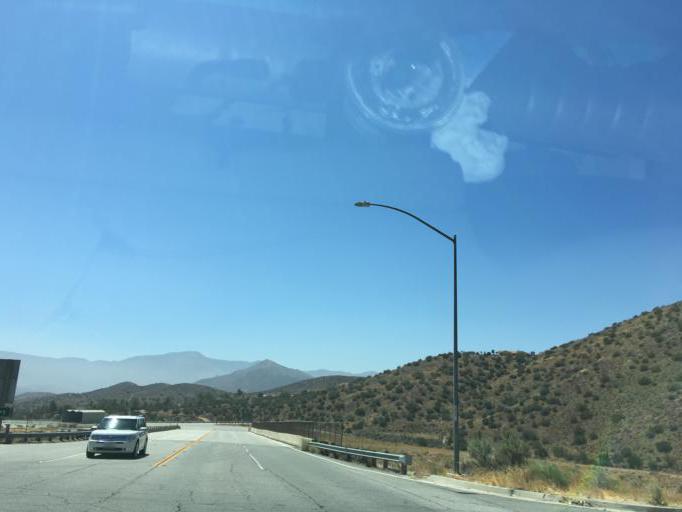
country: US
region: California
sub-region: Los Angeles County
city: Acton
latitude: 34.5015
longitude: -118.2284
